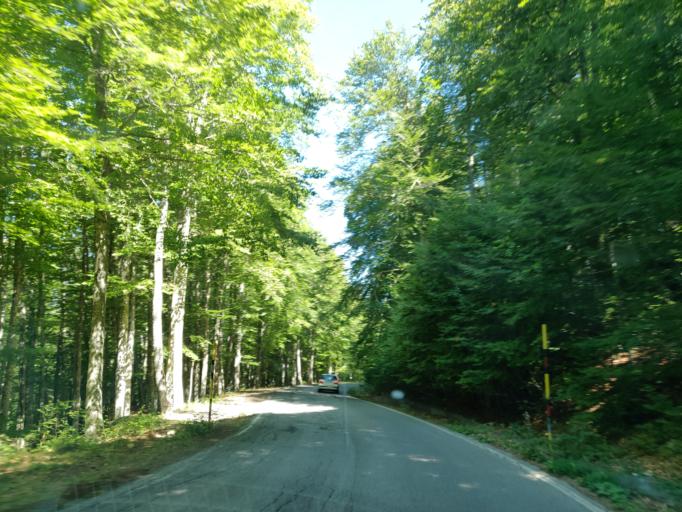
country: IT
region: Tuscany
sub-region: Provincia di Siena
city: Abbadia San Salvatore
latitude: 42.8957
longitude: 11.6133
